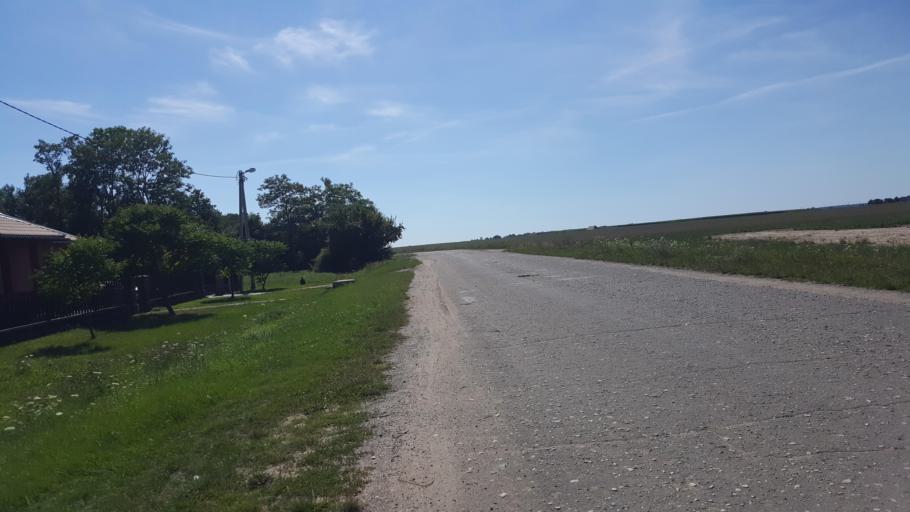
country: BY
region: Brest
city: Charnawchytsy
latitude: 52.2581
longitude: 23.5842
